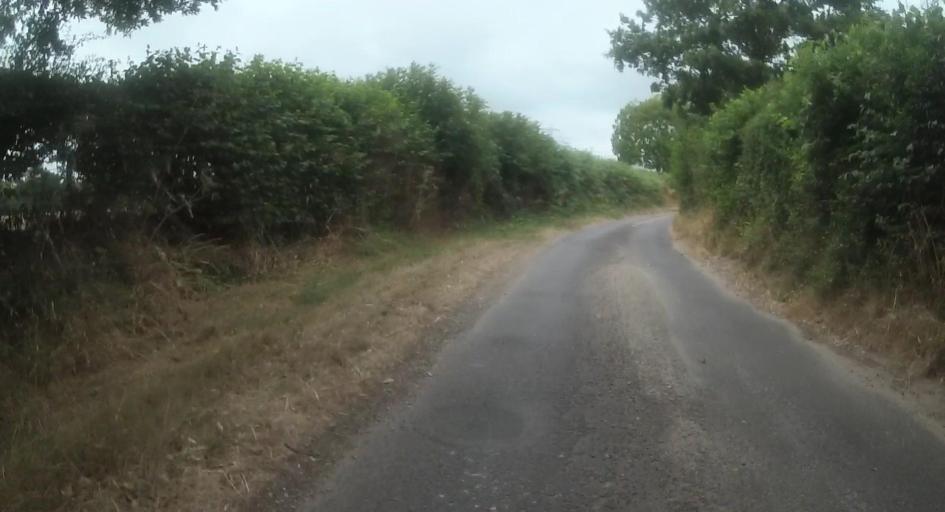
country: GB
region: England
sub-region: Dorset
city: Bovington Camp
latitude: 50.7247
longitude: -2.1972
